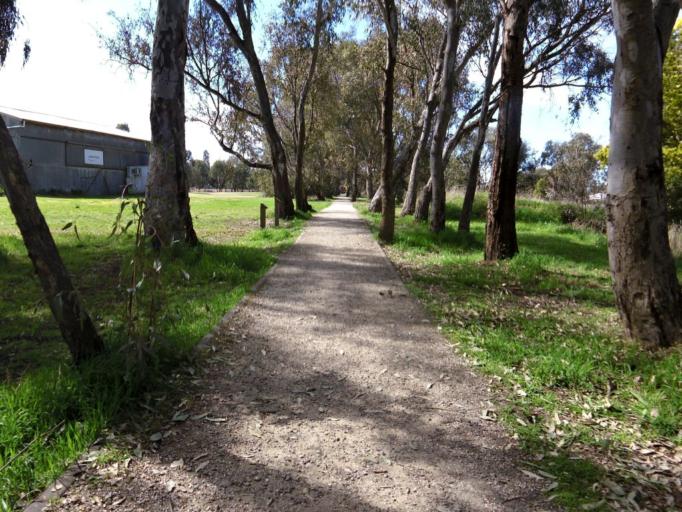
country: AU
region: Victoria
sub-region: Mansfield
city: Mansfield
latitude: -37.0503
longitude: 146.0806
